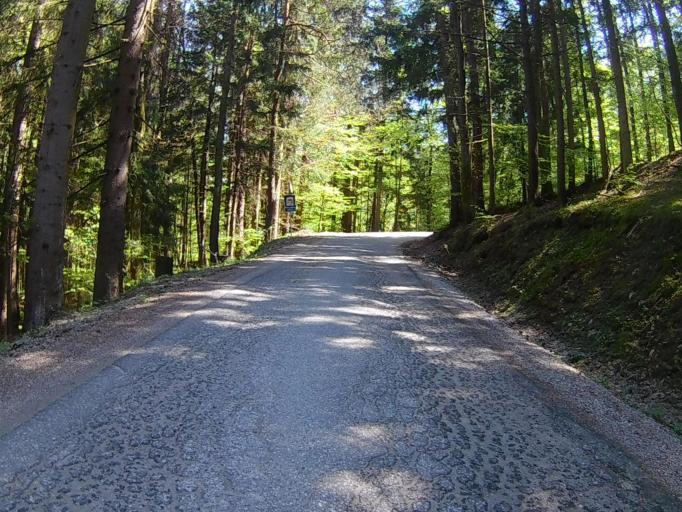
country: SI
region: Ruse
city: Ruse
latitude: 46.5249
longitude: 15.5156
